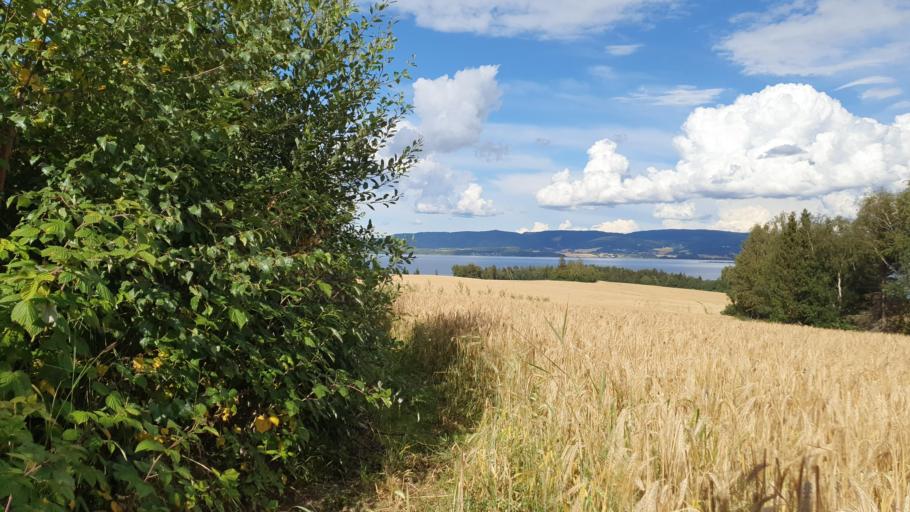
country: NO
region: Nord-Trondelag
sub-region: Levanger
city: Levanger
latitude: 63.7737
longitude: 11.3791
